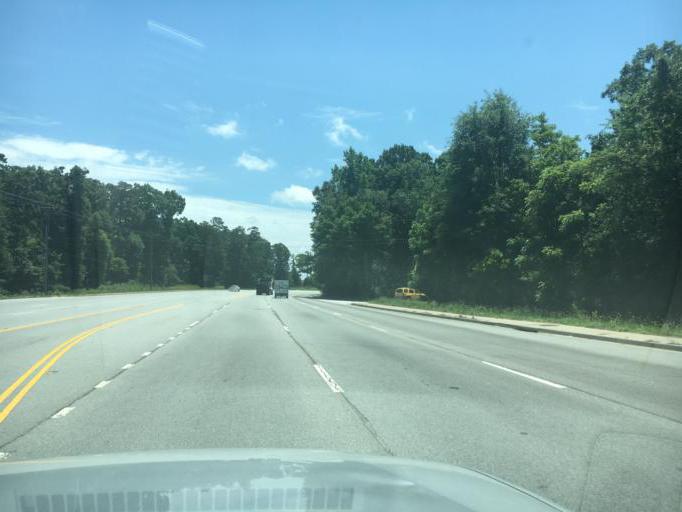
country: US
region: South Carolina
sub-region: Greenville County
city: Berea
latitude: 34.9140
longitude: -82.4616
